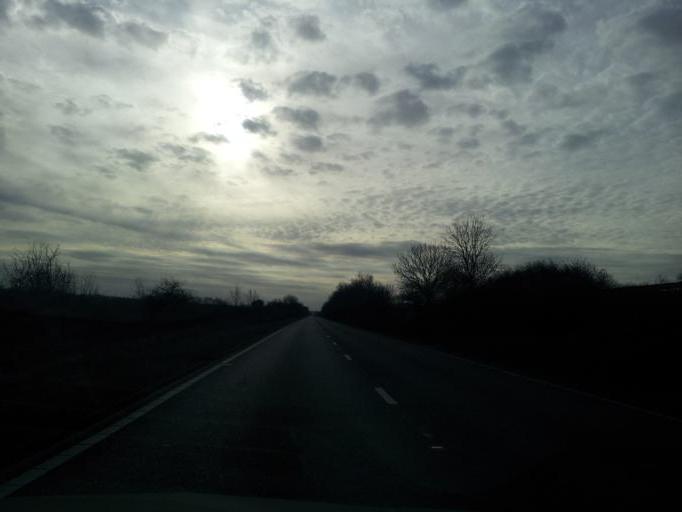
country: GB
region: England
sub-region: District of Rutland
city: Tickencote
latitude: 52.6847
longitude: -0.5501
